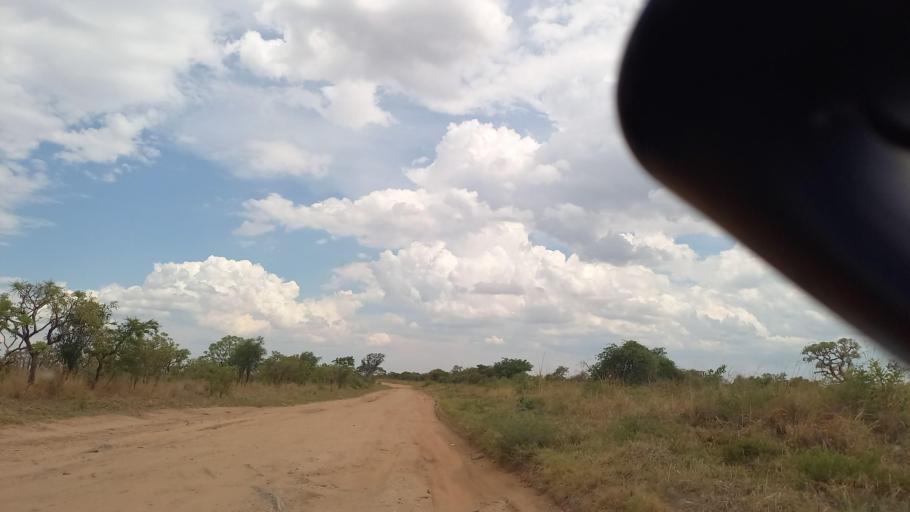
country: ZM
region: Southern
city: Nakambala
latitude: -16.0559
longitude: 27.9879
